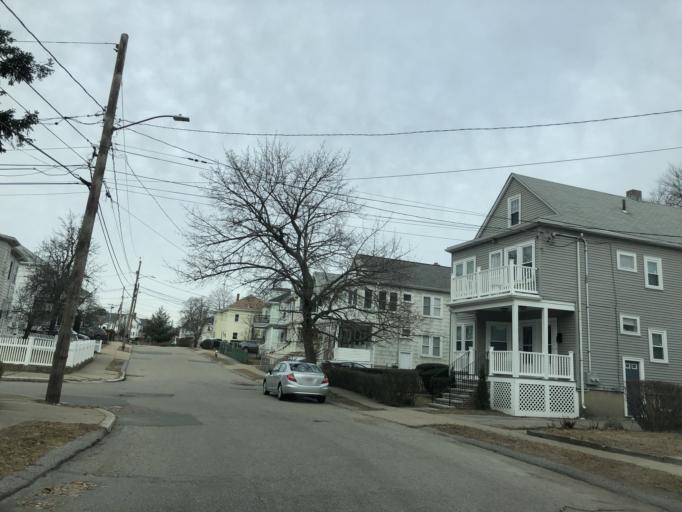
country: US
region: Massachusetts
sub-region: Middlesex County
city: Watertown
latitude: 42.3674
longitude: -71.1636
